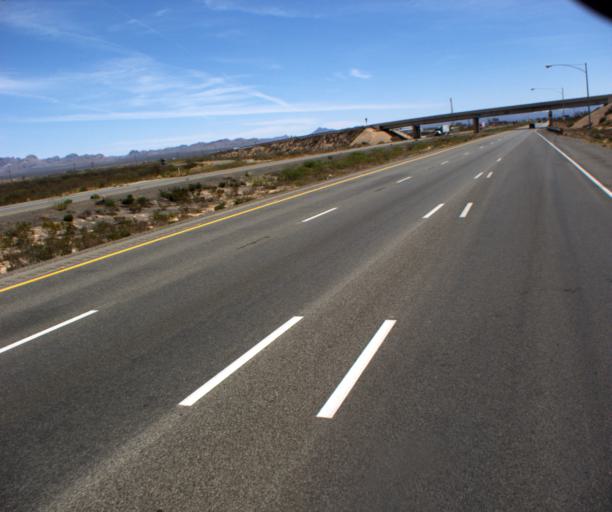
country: US
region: New Mexico
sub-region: Hidalgo County
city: Lordsburg
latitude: 32.2725
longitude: -109.2516
